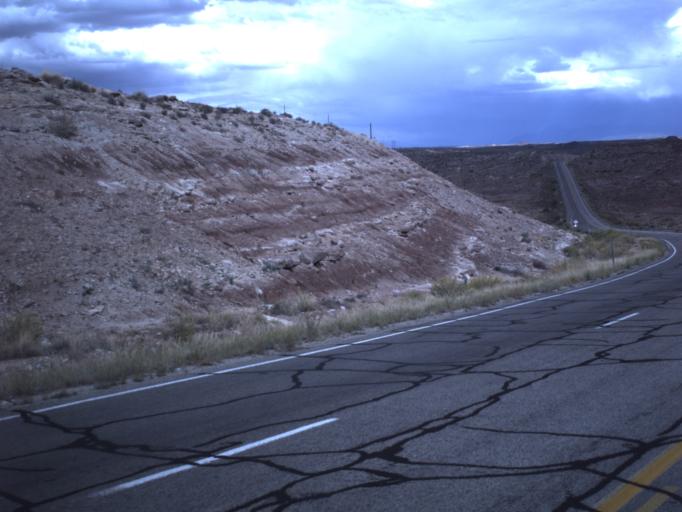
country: US
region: Utah
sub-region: San Juan County
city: Blanding
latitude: 37.2743
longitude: -109.3585
